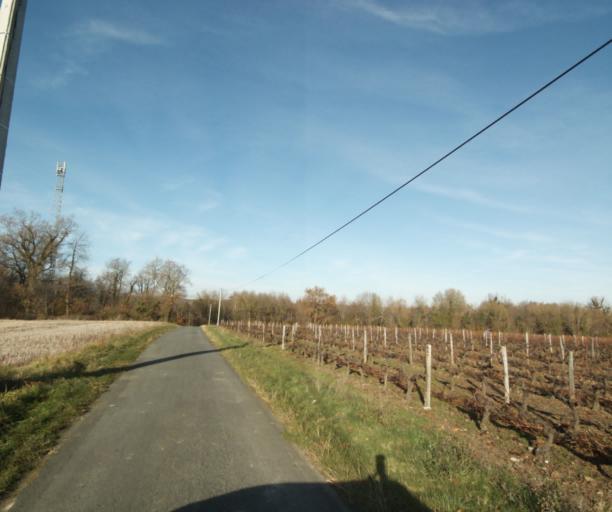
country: FR
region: Poitou-Charentes
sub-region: Departement de la Charente-Maritime
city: Ecoyeux
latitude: 45.7586
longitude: -0.4953
